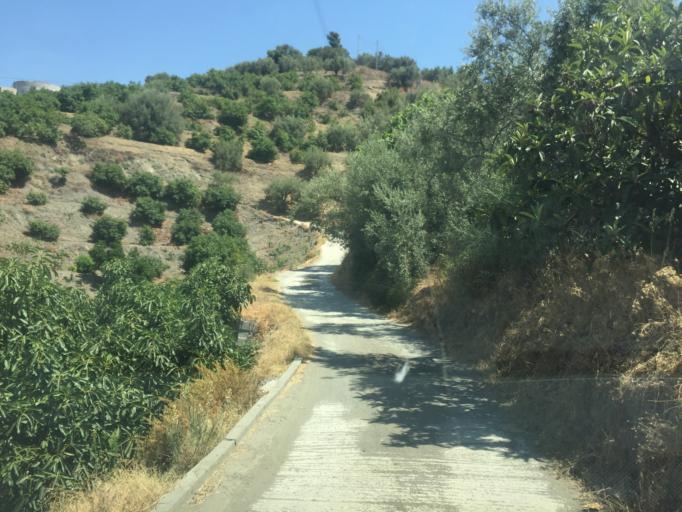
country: ES
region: Andalusia
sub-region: Provincia de Malaga
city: Competa
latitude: 36.8073
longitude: -3.9367
